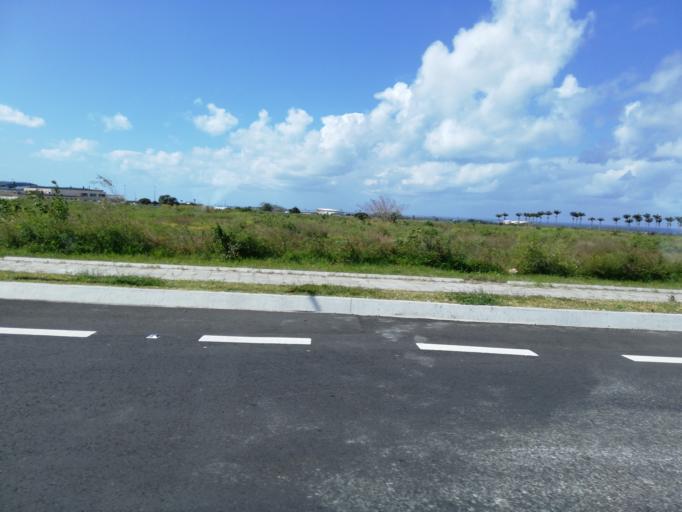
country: MU
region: Grand Port
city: Plaine Magnien
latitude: -20.4391
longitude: 57.6716
